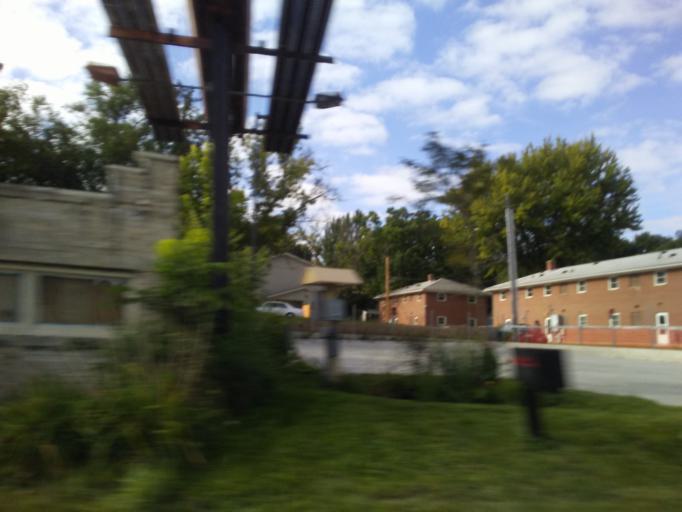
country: US
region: Wisconsin
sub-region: Dane County
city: Shorewood Hills
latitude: 43.0749
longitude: -89.4397
